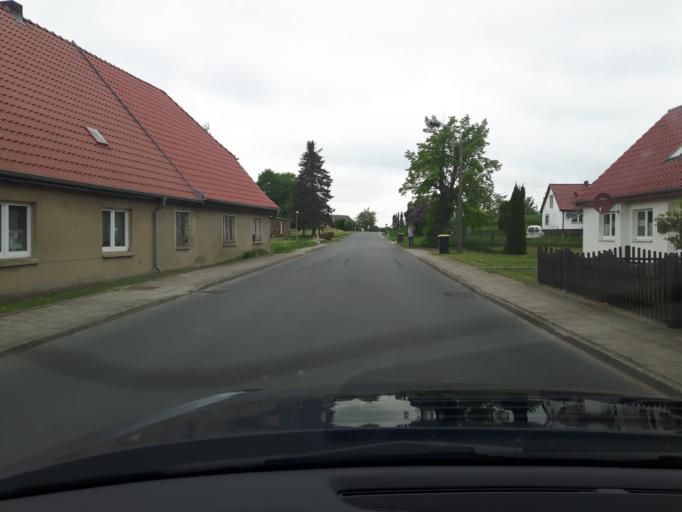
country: DE
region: Mecklenburg-Vorpommern
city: Gnoien
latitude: 54.0161
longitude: 12.6564
